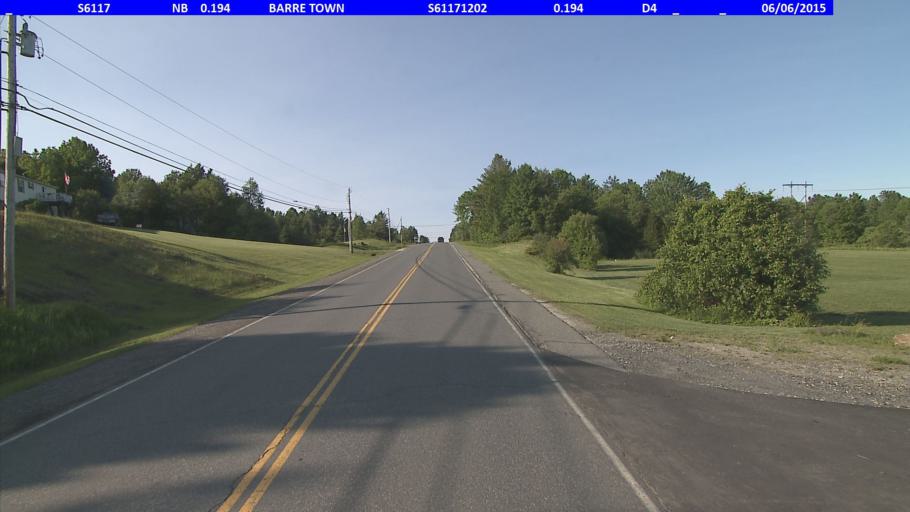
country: US
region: Vermont
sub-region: Washington County
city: Barre
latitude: 44.1916
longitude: -72.5228
